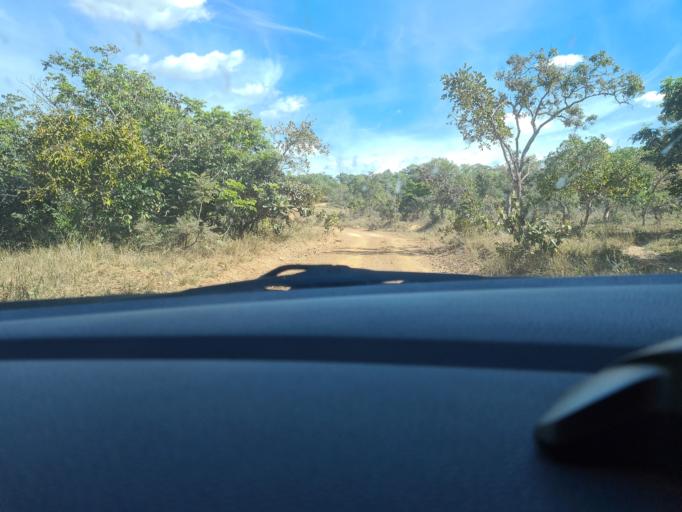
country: BR
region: Goias
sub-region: Silvania
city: Silvania
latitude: -16.5275
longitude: -48.5410
